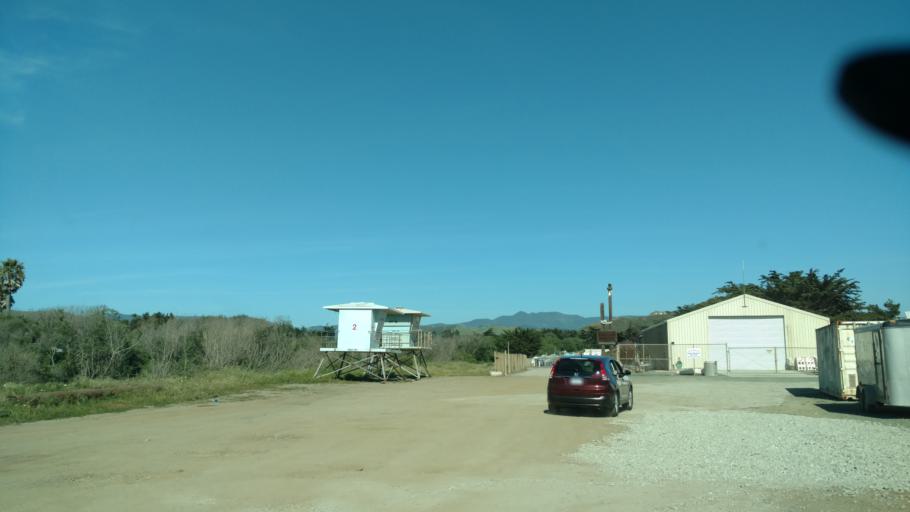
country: US
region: California
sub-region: San Luis Obispo County
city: Morro Bay
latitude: 35.3758
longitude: -120.8615
